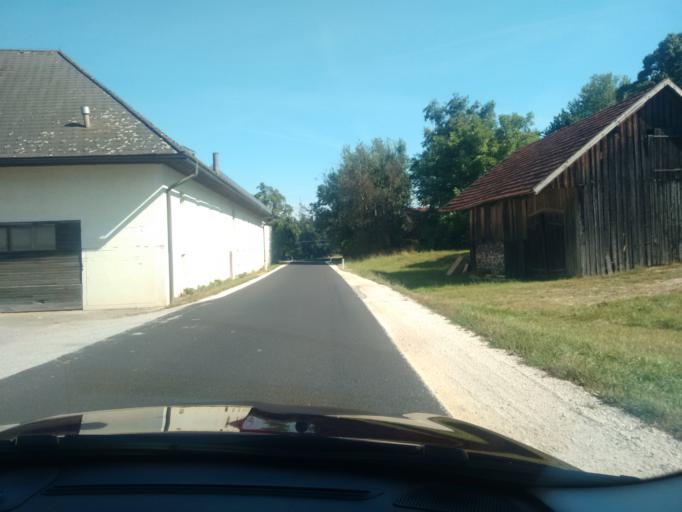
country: AT
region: Upper Austria
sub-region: Wels-Land
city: Sattledt
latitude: 48.0814
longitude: 14.0712
